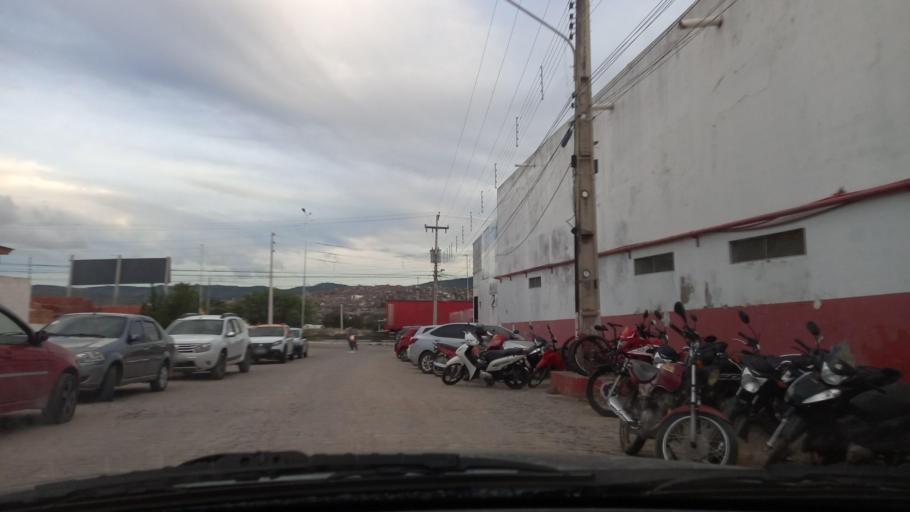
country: BR
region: Pernambuco
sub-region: Gravata
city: Gravata
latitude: -8.1951
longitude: -35.5698
